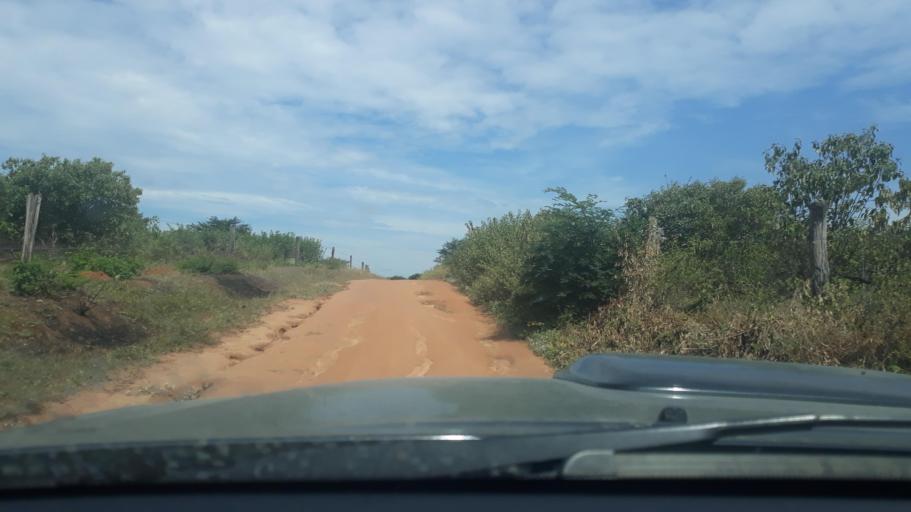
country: BR
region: Bahia
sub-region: Riacho De Santana
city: Riacho de Santana
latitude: -13.8576
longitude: -43.0632
